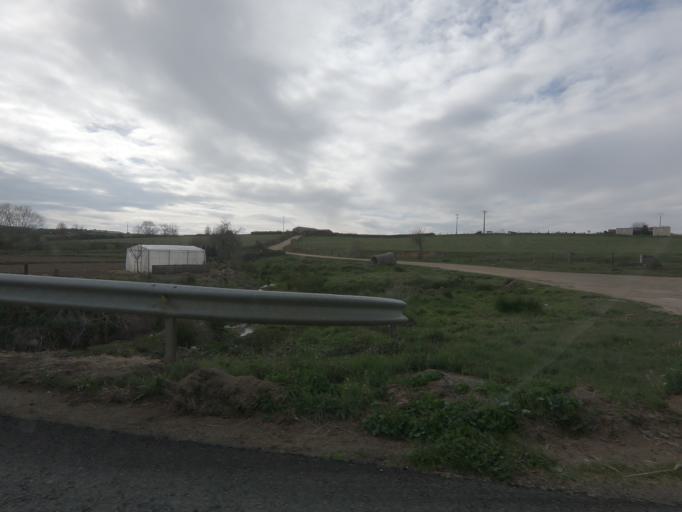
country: ES
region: Castille and Leon
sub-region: Provincia de Salamanca
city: Villasrubias
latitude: 40.3412
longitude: -6.6392
